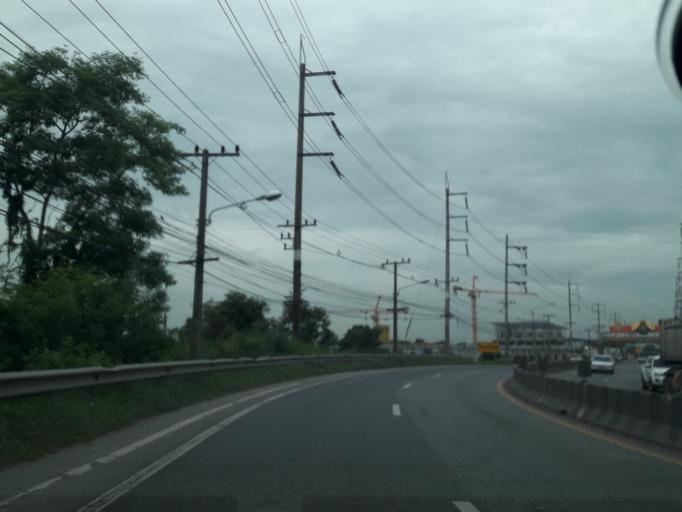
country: TH
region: Pathum Thani
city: Lam Luk Ka
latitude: 13.9411
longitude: 100.7669
